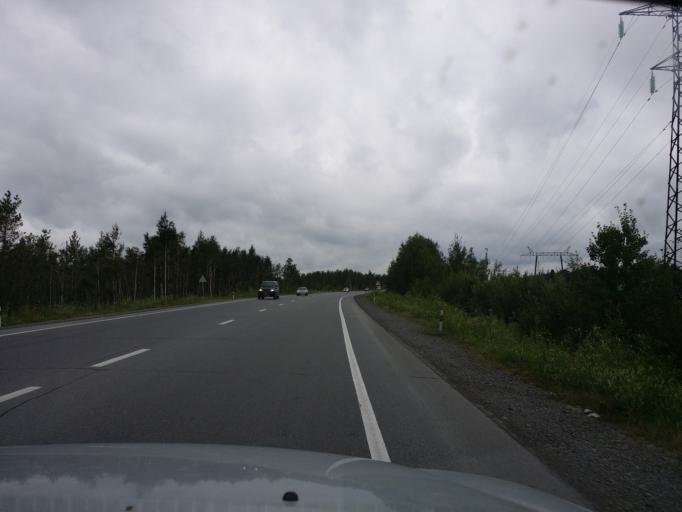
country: RU
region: Khanty-Mansiyskiy Avtonomnyy Okrug
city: Nizhnevartovsk
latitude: 61.0440
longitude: 76.3490
